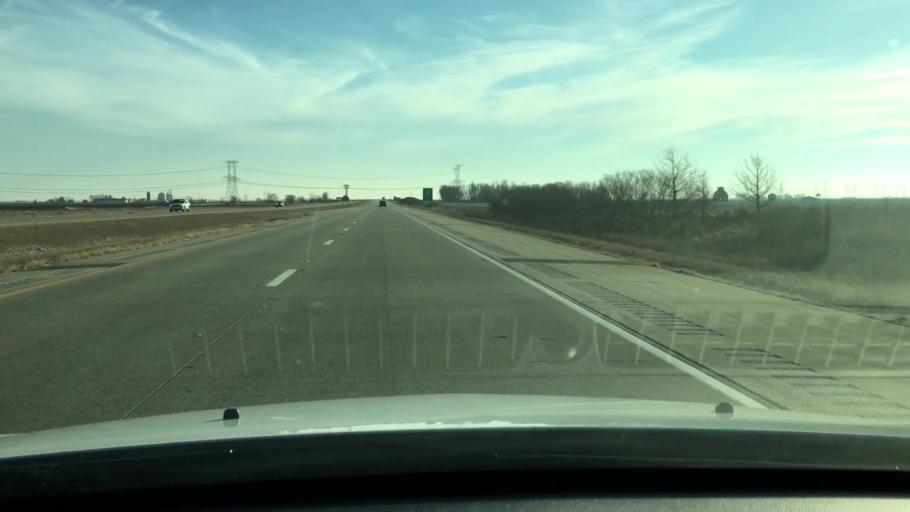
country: US
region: Illinois
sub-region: Woodford County
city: Minonk
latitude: 40.8752
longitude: -89.0368
